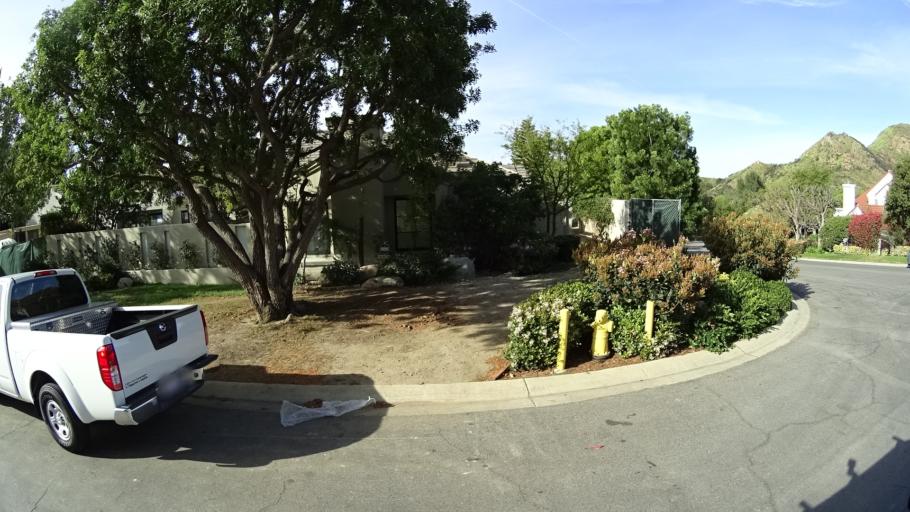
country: US
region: California
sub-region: Ventura County
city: Oak Park
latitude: 34.1979
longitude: -118.7857
